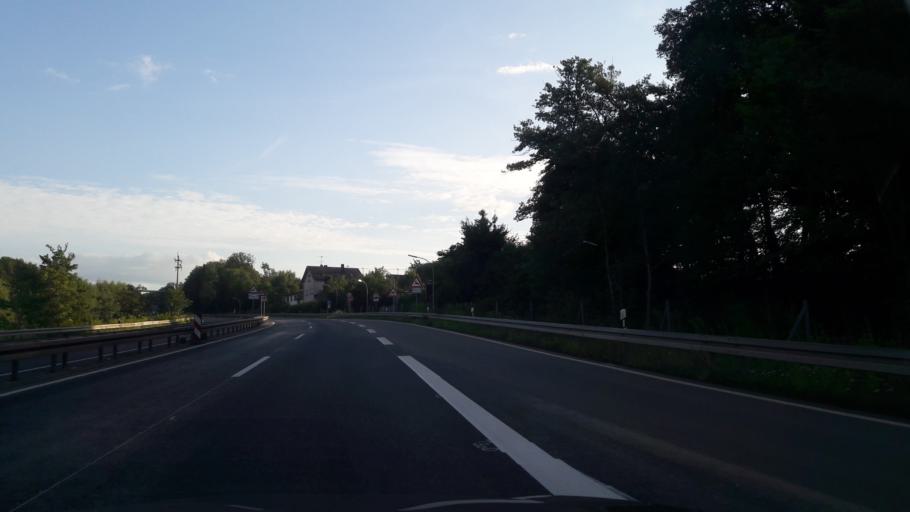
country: DE
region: Saarland
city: Riegelsberg
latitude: 49.2763
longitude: 6.9626
